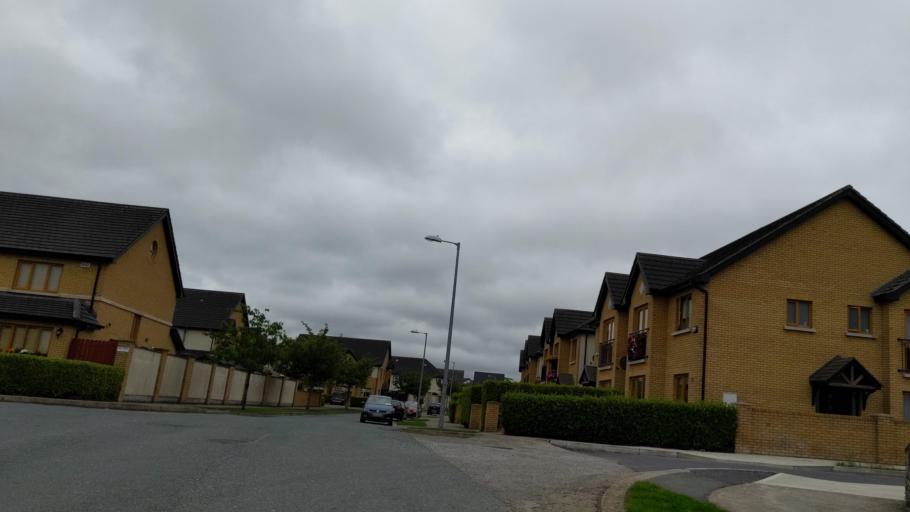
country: IE
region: Leinster
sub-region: Lu
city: Drogheda
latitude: 53.7039
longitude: -6.3538
